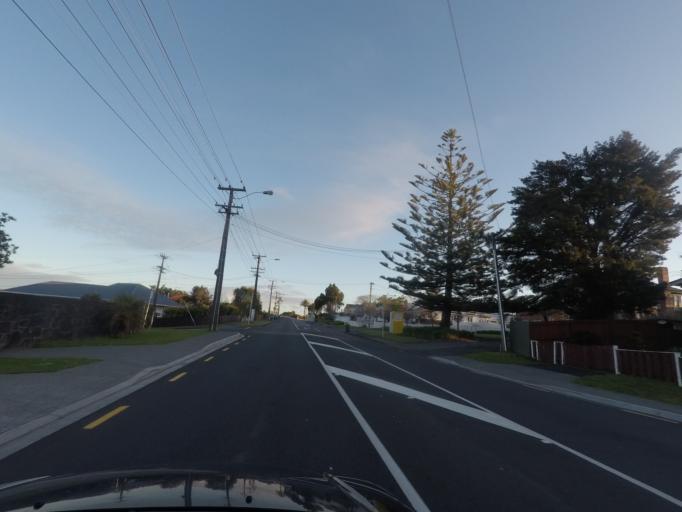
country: NZ
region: Auckland
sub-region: Auckland
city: Rosebank
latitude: -36.8830
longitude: 174.6458
